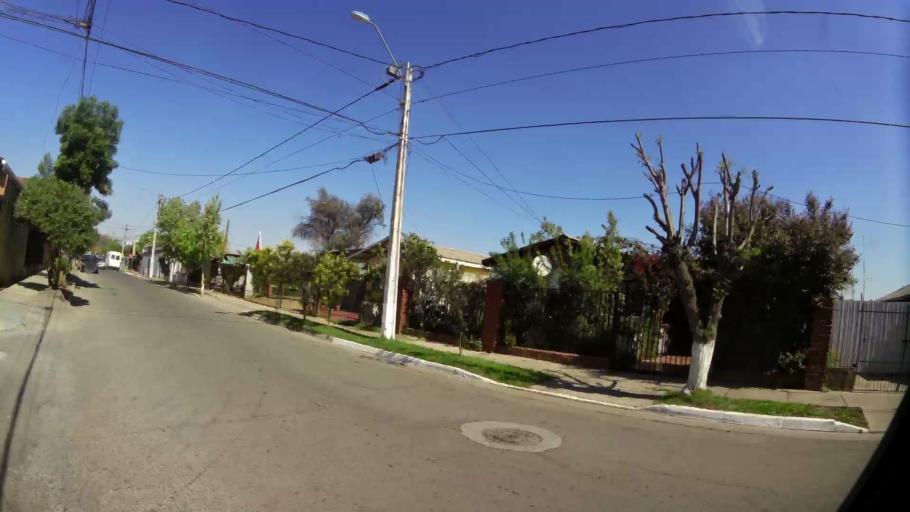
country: CL
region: Santiago Metropolitan
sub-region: Provincia de Talagante
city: Penaflor
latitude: -33.5689
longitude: -70.8069
